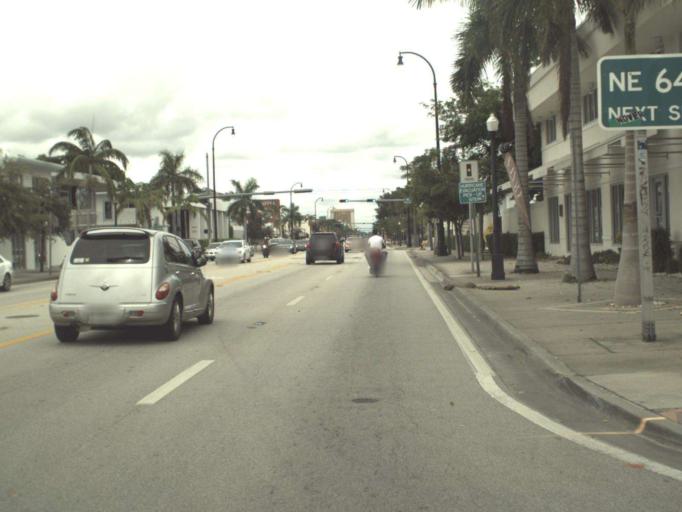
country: US
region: Florida
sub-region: Miami-Dade County
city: El Portal
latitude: 25.8340
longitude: -80.1840
